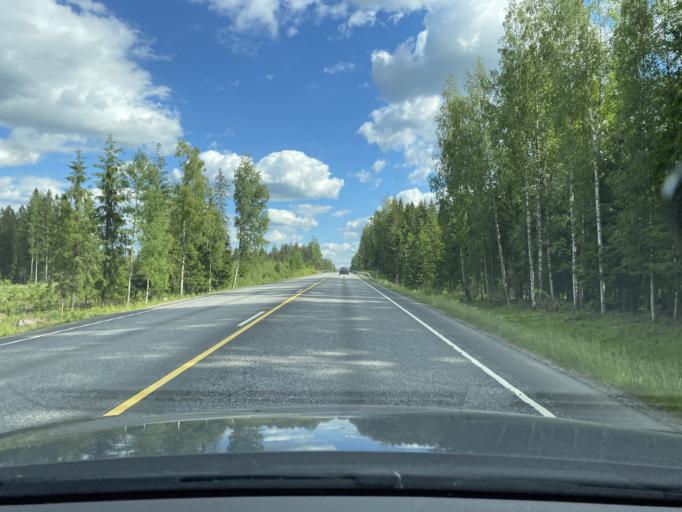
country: FI
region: Varsinais-Suomi
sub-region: Loimaa
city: Alastaro
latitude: 61.0821
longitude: 22.9004
